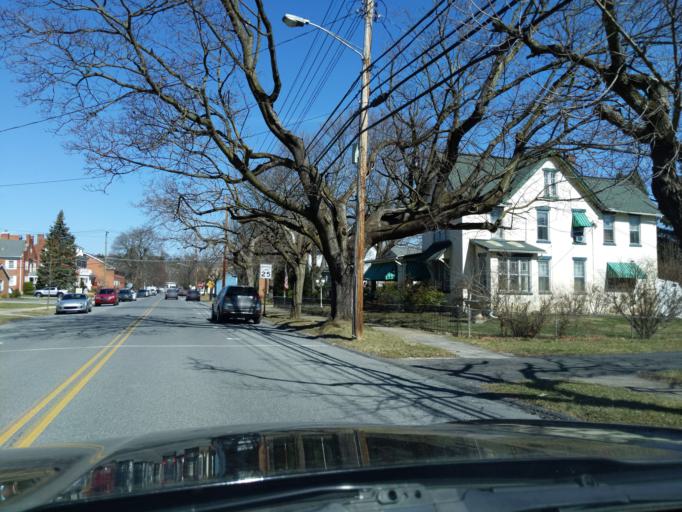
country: US
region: Pennsylvania
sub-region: Blair County
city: Hollidaysburg
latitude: 40.4243
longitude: -78.3996
